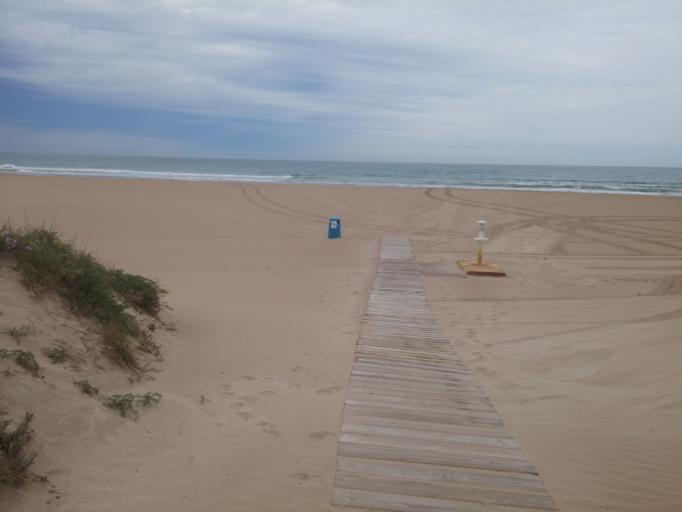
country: ES
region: Valencia
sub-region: Provincia de Valencia
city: Oliva
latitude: 38.9038
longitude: -0.0623
